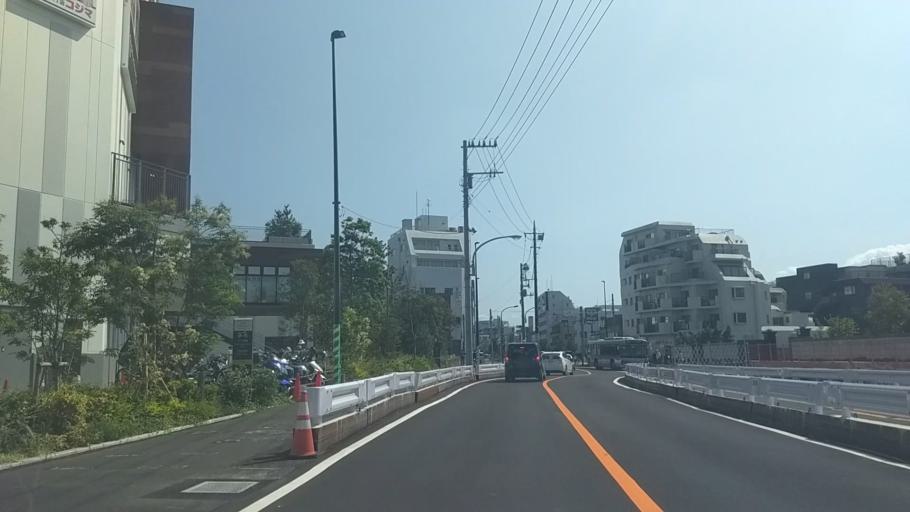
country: JP
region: Kanagawa
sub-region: Kawasaki-shi
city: Kawasaki
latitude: 35.5751
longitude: 139.7259
